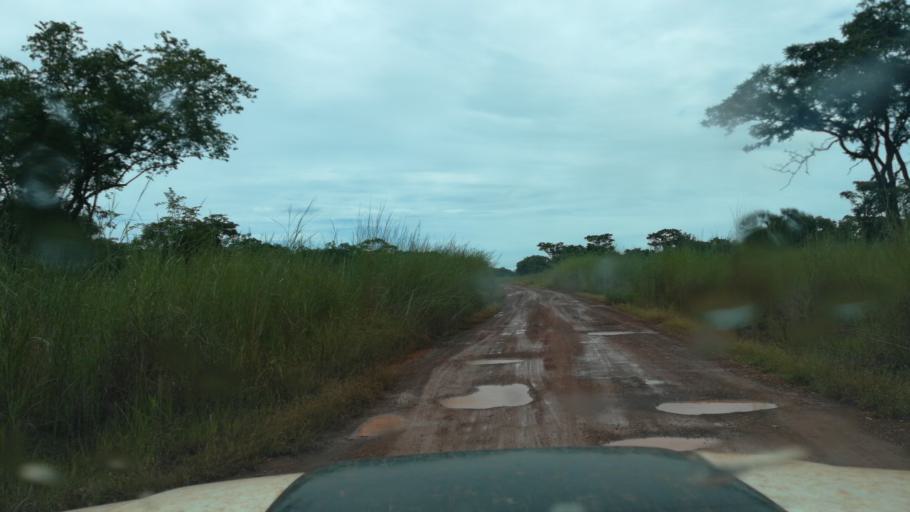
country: ZM
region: Luapula
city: Mwense
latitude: -10.0306
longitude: 28.1193
